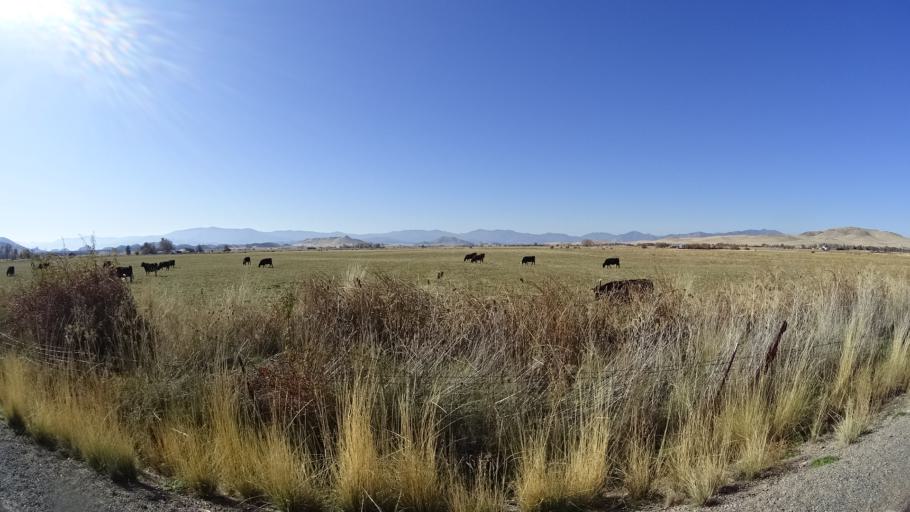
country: US
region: California
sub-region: Siskiyou County
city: Montague
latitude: 41.7152
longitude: -122.3892
